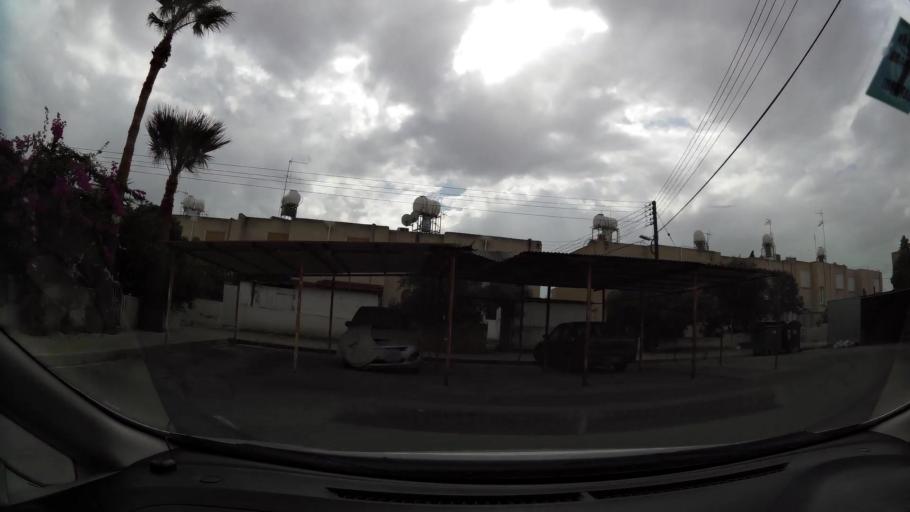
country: CY
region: Lefkosia
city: Geri
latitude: 35.1160
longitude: 33.3846
